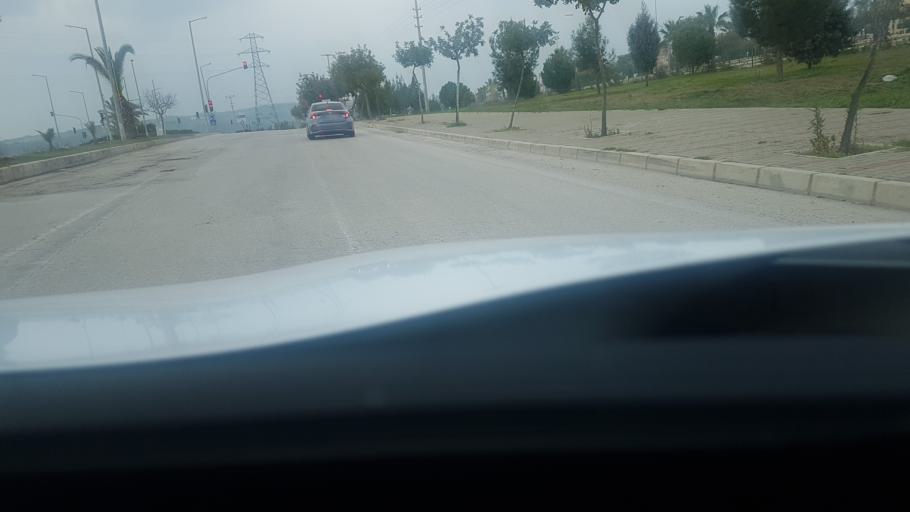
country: TR
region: Adana
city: Seyhan
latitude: 37.0566
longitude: 35.2465
